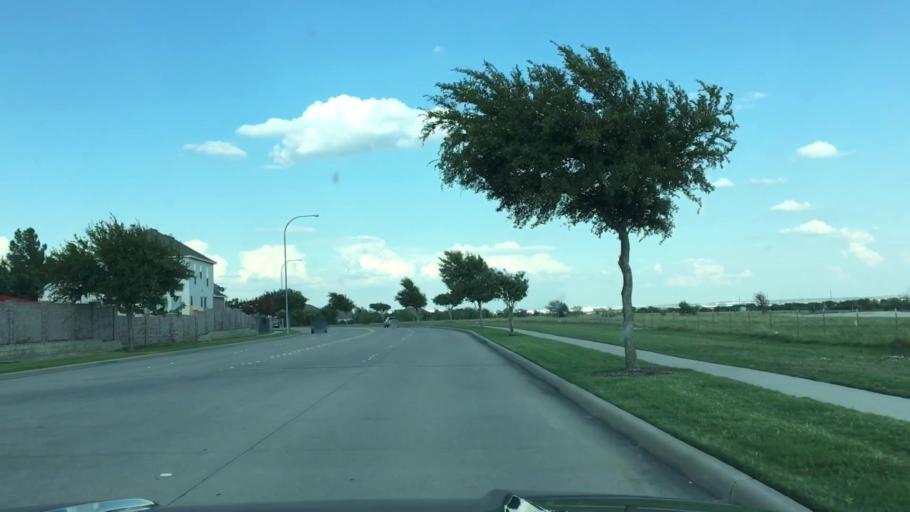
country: US
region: Texas
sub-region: Tarrant County
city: Haslet
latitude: 32.9838
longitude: -97.3790
